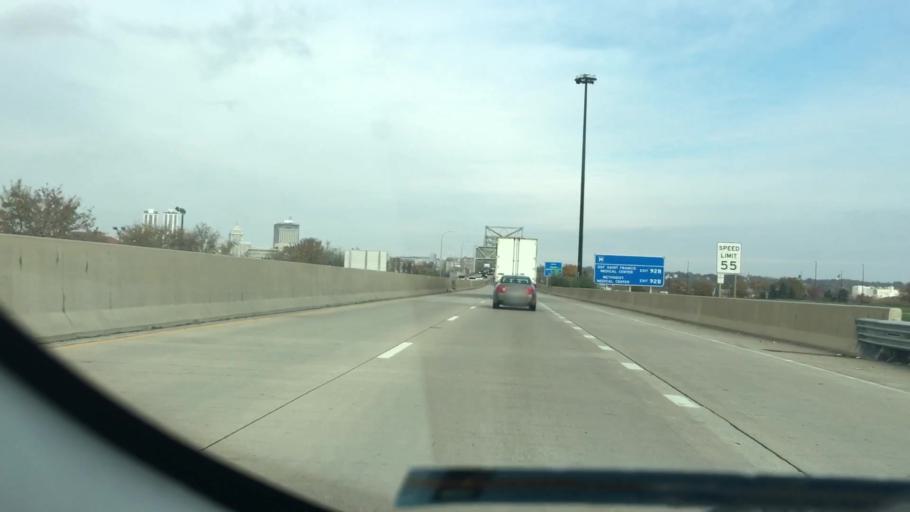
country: US
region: Illinois
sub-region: Peoria County
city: Peoria
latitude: 40.6827
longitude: -89.5815
